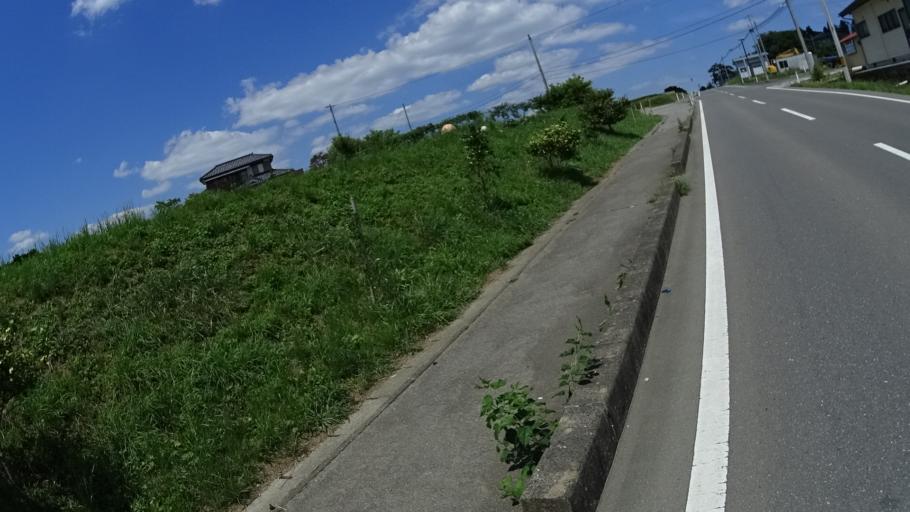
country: JP
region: Iwate
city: Ofunato
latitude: 38.8452
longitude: 141.6182
